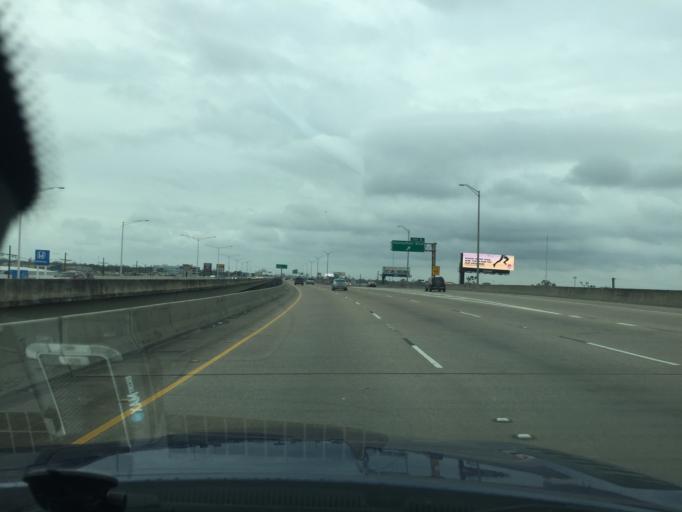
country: US
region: Louisiana
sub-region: Jefferson Parish
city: Harvey
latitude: 29.9004
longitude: -90.0718
